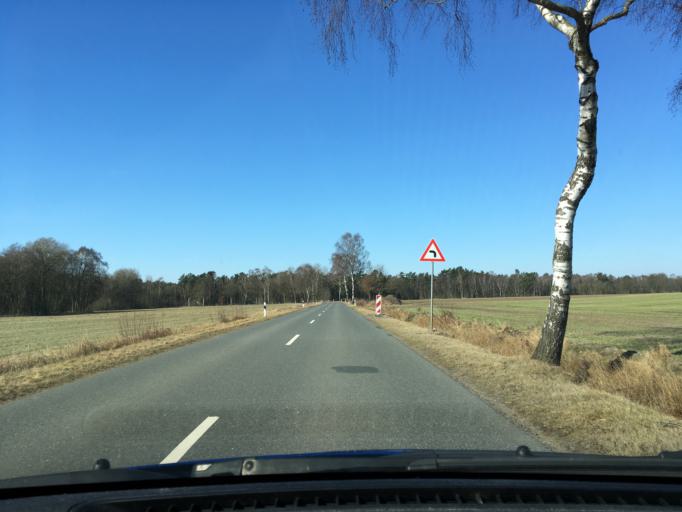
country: DE
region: Lower Saxony
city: Schneverdingen
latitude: 53.0830
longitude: 9.8432
